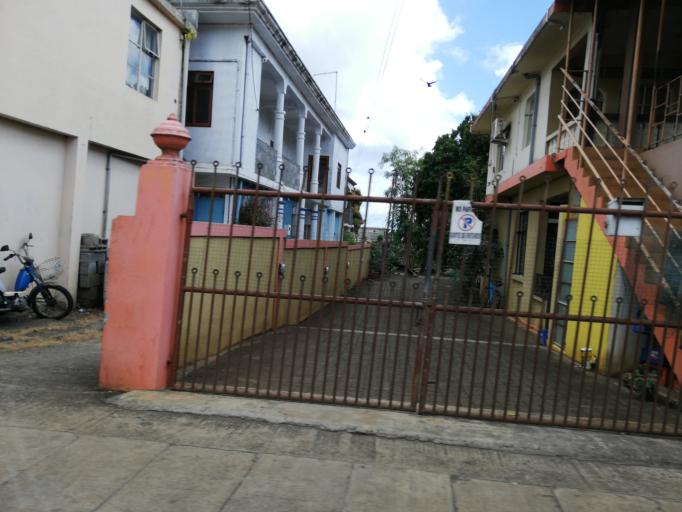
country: MU
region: Pamplemousses
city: Triolet
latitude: -20.0564
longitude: 57.5524
